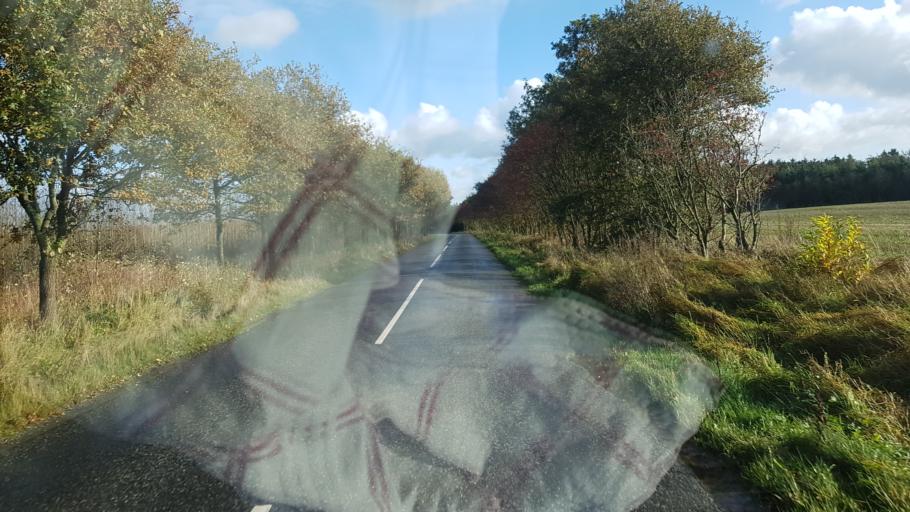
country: DK
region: South Denmark
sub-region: Varde Kommune
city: Olgod
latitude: 55.6976
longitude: 8.7238
